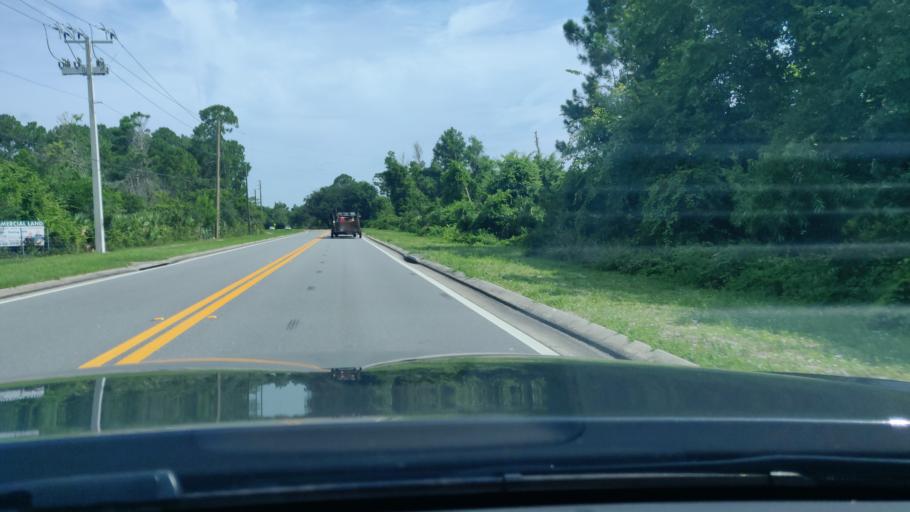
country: US
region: Florida
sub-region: Flagler County
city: Palm Coast
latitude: 29.5436
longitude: -81.1756
